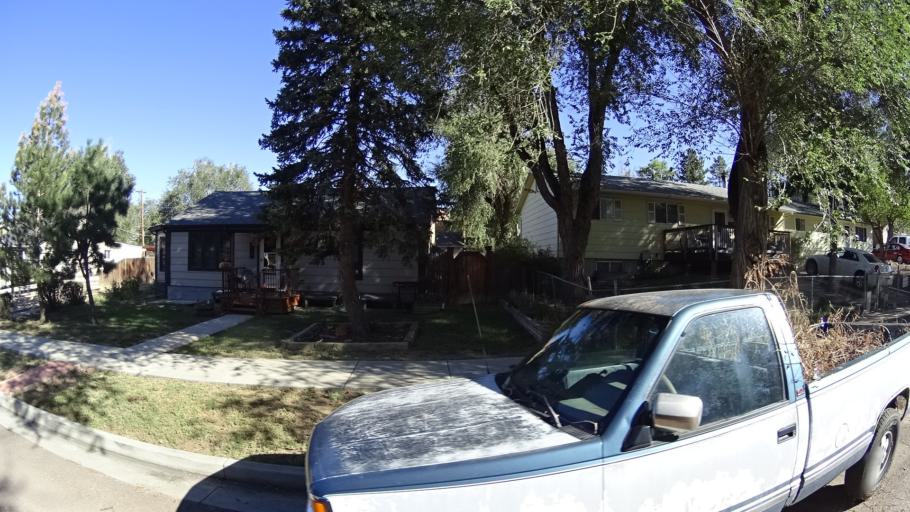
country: US
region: Colorado
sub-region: El Paso County
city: Colorado Springs
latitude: 38.8471
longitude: -104.8465
